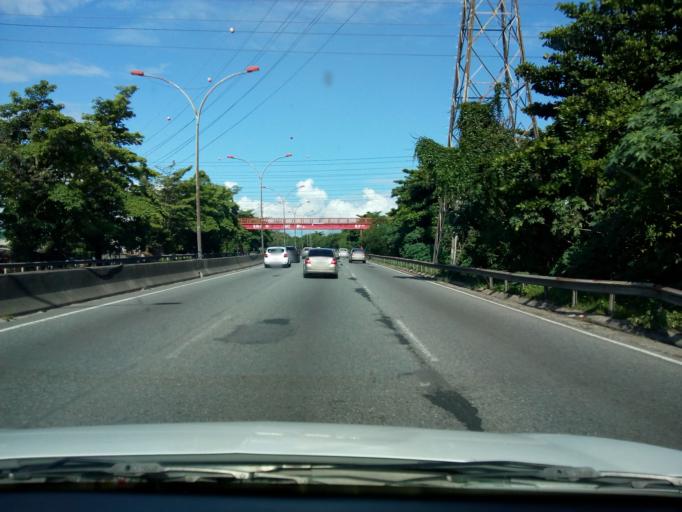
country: BR
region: Rio de Janeiro
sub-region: Duque De Caxias
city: Duque de Caxias
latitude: -22.8024
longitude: -43.3324
